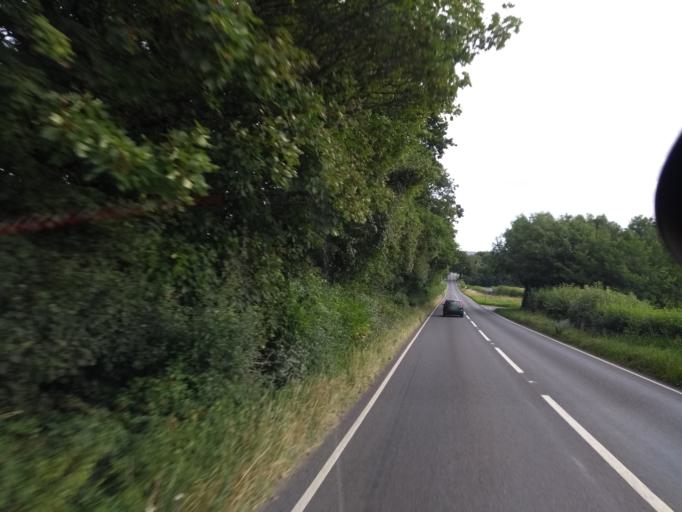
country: GB
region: England
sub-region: Somerset
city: Crewkerne
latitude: 50.8574
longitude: -2.7722
